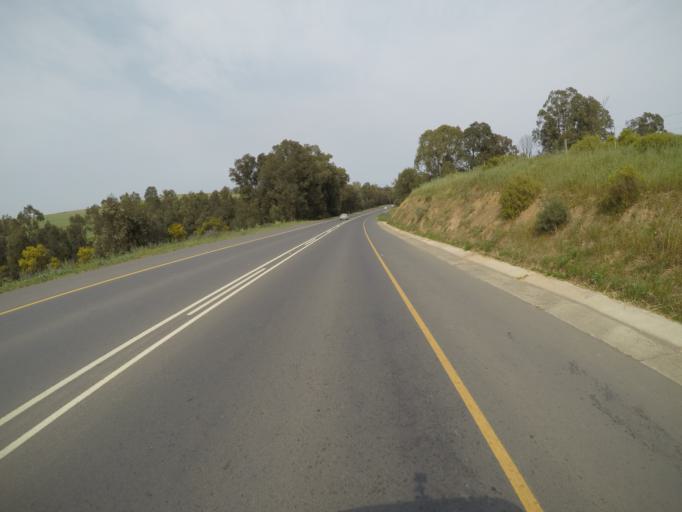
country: ZA
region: Western Cape
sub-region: West Coast District Municipality
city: Malmesbury
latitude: -33.4569
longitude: 18.7474
